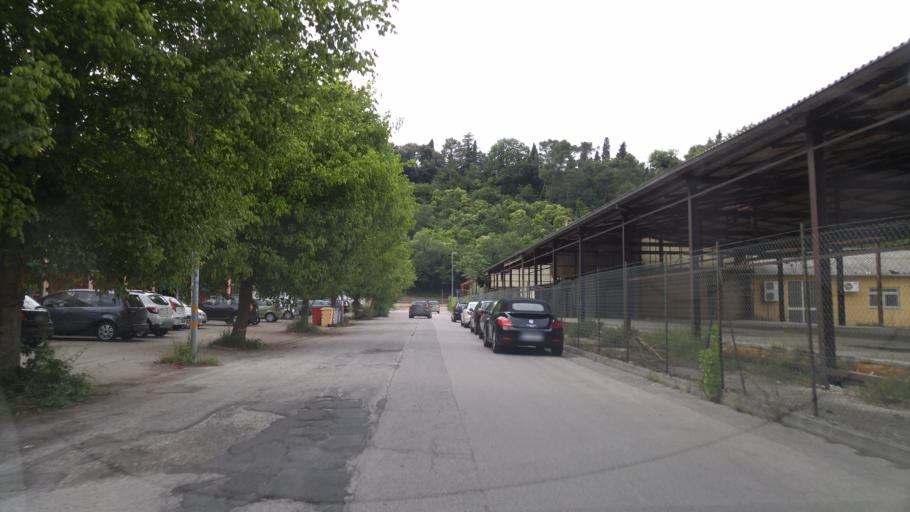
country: IT
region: The Marches
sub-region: Provincia di Pesaro e Urbino
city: Pesaro
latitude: 43.9069
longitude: 12.8655
